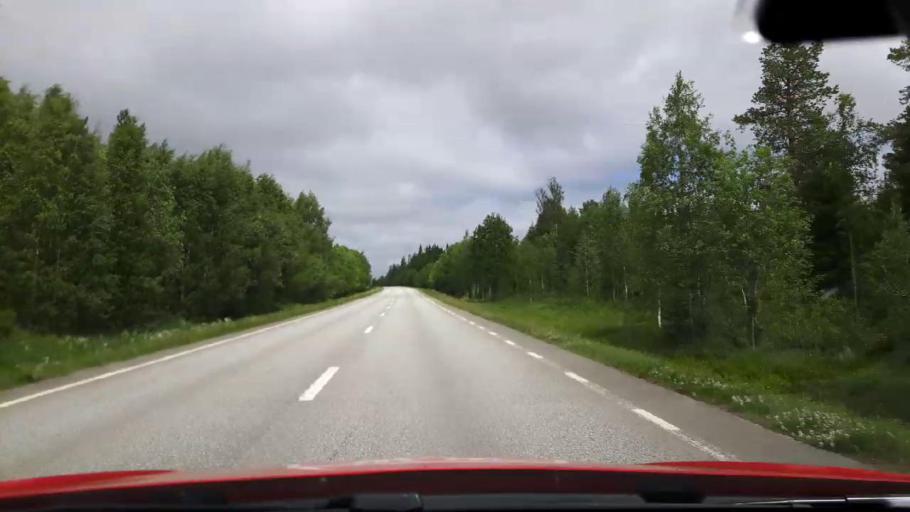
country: SE
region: Jaemtland
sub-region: Krokoms Kommun
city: Krokom
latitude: 63.4977
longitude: 14.5106
